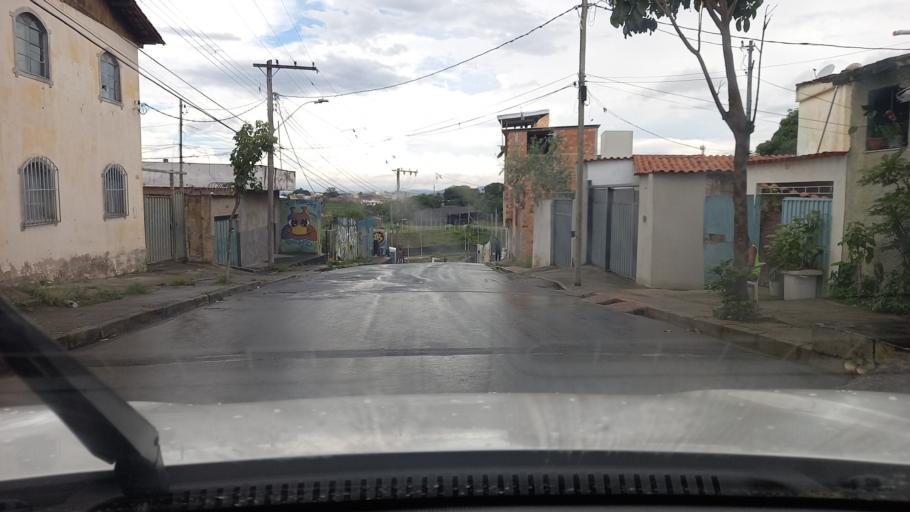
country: BR
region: Minas Gerais
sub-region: Belo Horizonte
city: Belo Horizonte
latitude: -19.9001
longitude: -43.9485
